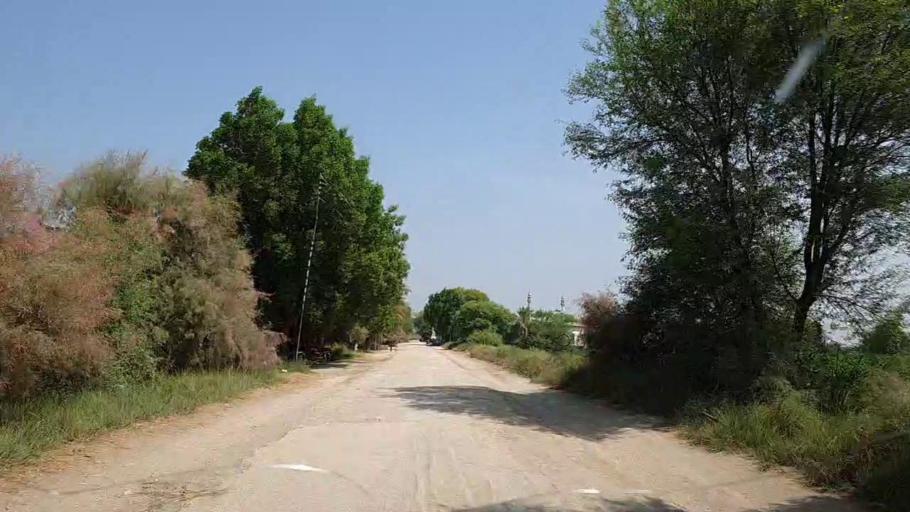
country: PK
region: Sindh
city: Adilpur
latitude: 27.8278
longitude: 69.2963
